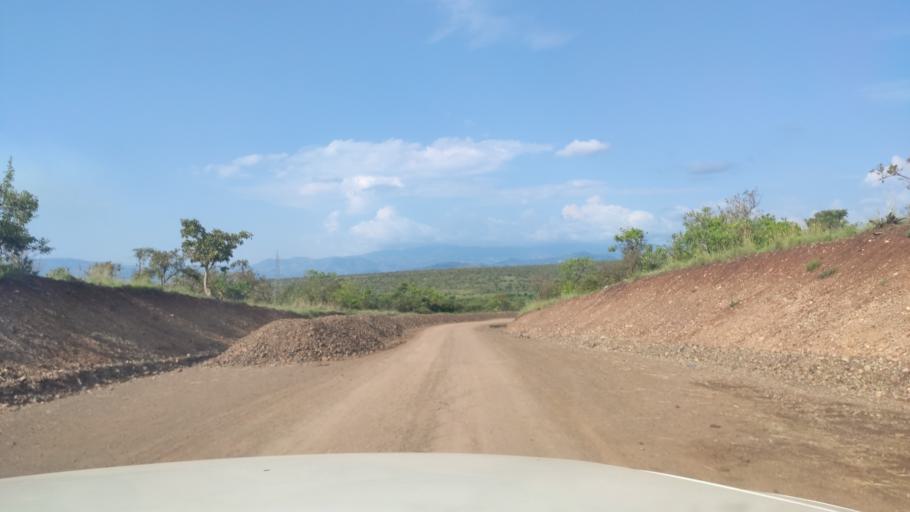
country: ET
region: Southern Nations, Nationalities, and People's Region
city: Felege Neway
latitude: 6.4321
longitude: 37.2647
